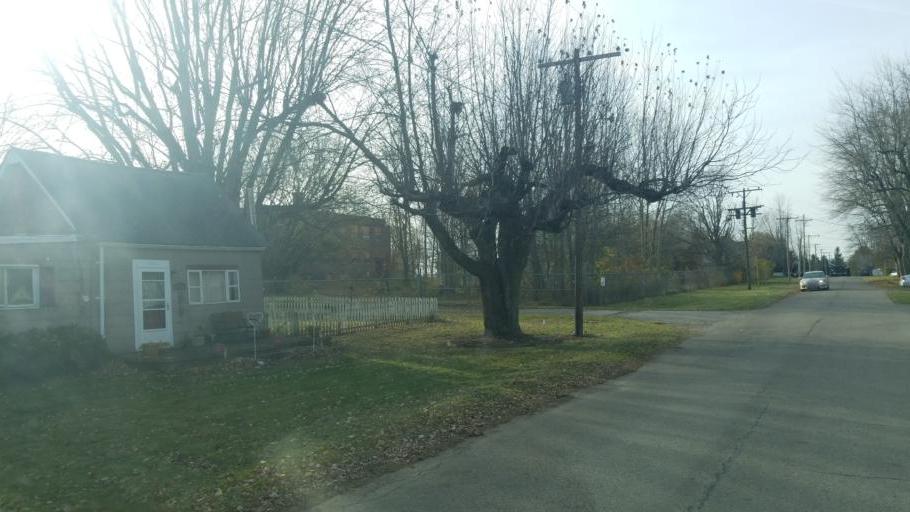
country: US
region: Ohio
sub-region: Madison County
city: Plain City
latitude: 40.1375
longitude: -83.3402
